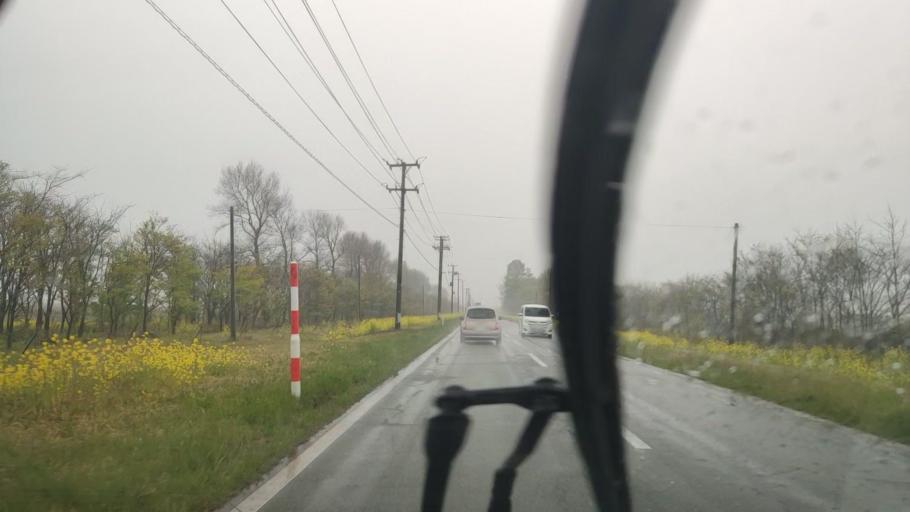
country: JP
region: Akita
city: Tenno
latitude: 39.9776
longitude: 139.9462
